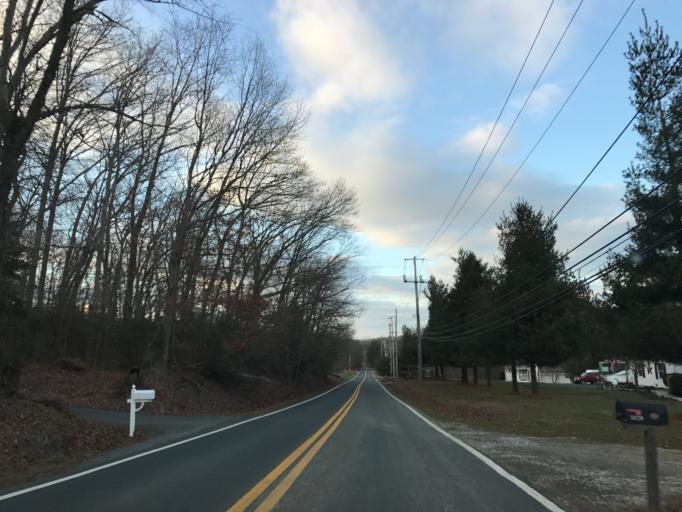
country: US
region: Maryland
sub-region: Cecil County
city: Charlestown
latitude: 39.5147
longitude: -75.9521
